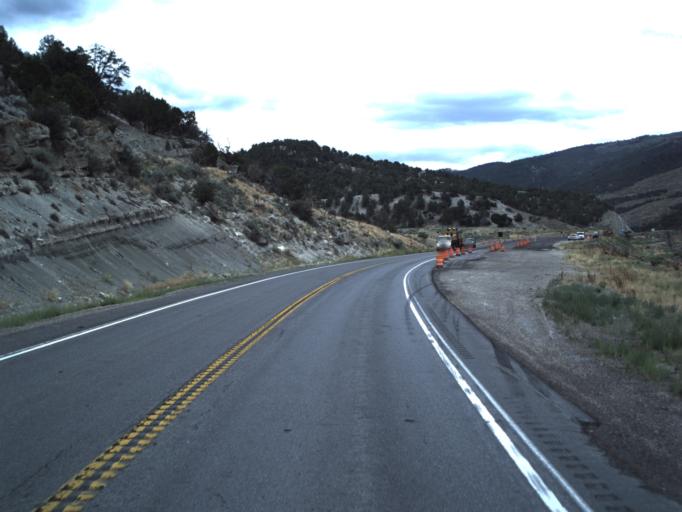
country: US
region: Utah
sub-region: Utah County
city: Mapleton
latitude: 39.9653
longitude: -111.3091
